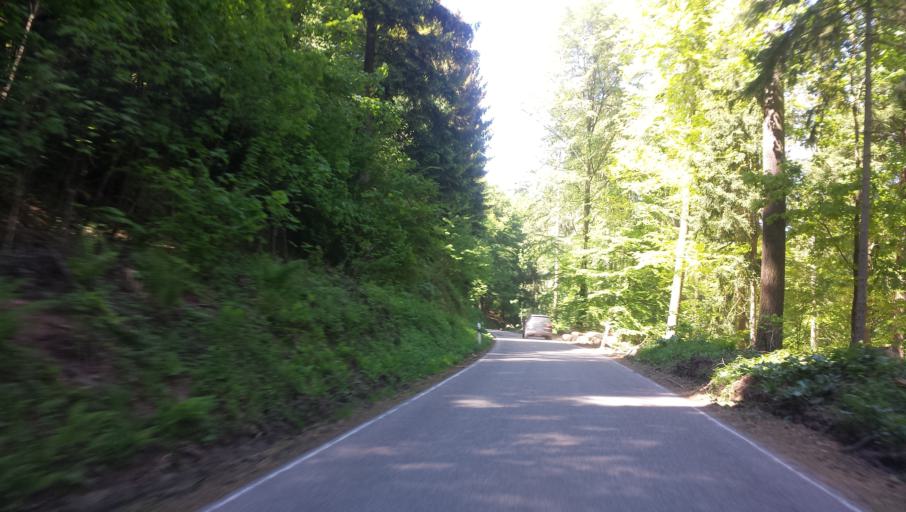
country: DE
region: Rheinland-Pfalz
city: Ramberg
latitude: 49.2749
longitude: 8.0278
